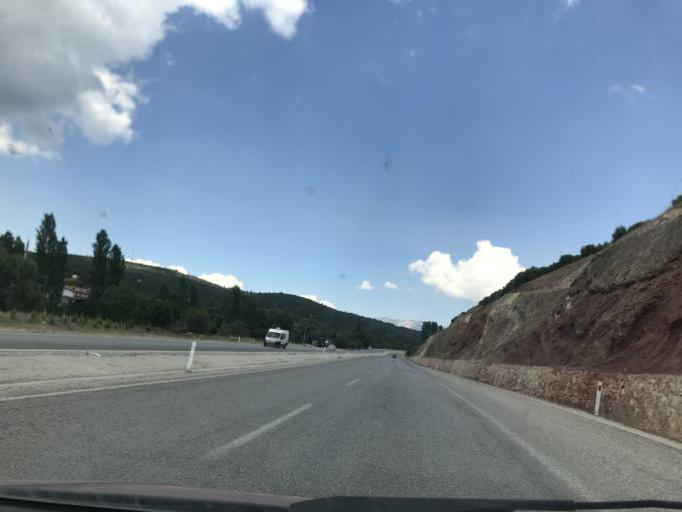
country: TR
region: Denizli
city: Tavas
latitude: 37.6061
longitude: 29.1322
